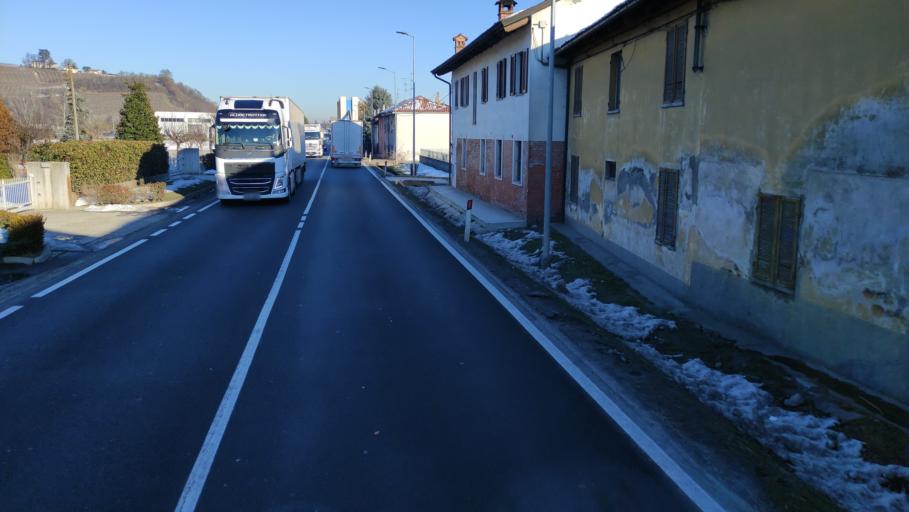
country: IT
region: Piedmont
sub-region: Provincia di Cuneo
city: Borgo
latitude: 44.7062
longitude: 7.9930
